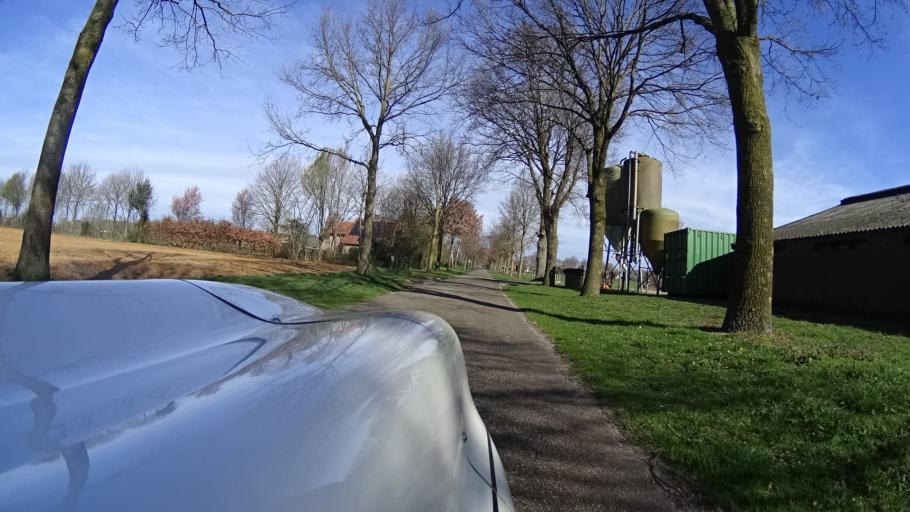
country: NL
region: North Brabant
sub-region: Gemeente Mill en Sint Hubert
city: Wilbertoord
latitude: 51.6840
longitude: 5.7506
